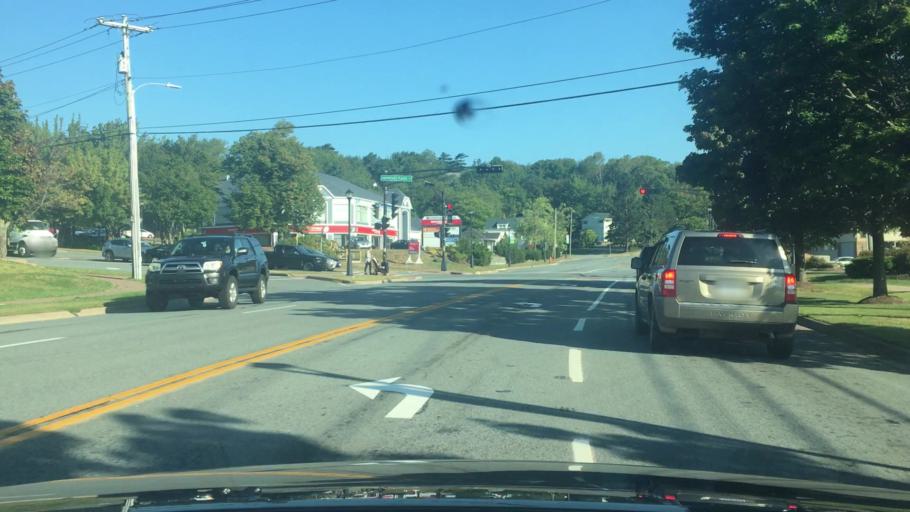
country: CA
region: Nova Scotia
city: Dartmouth
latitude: 44.7147
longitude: -63.6781
